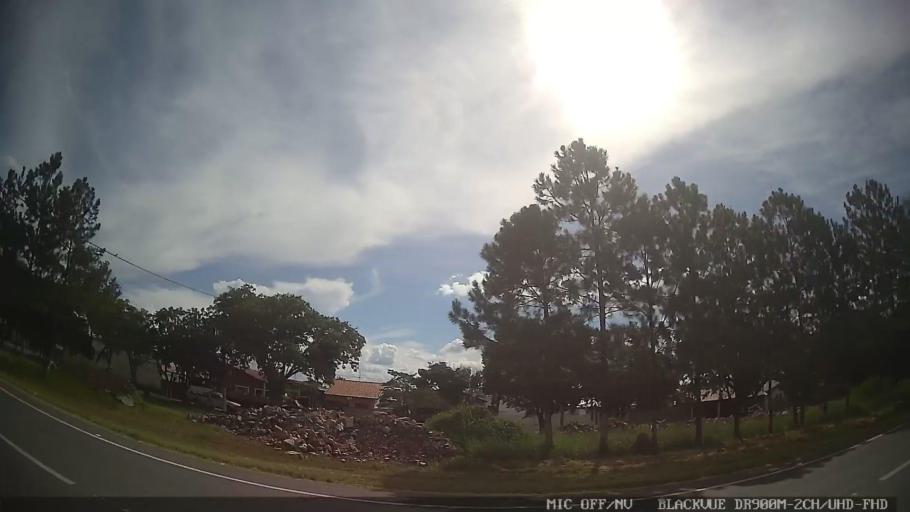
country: BR
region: Sao Paulo
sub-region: Conchas
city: Conchas
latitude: -23.0699
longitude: -47.9734
